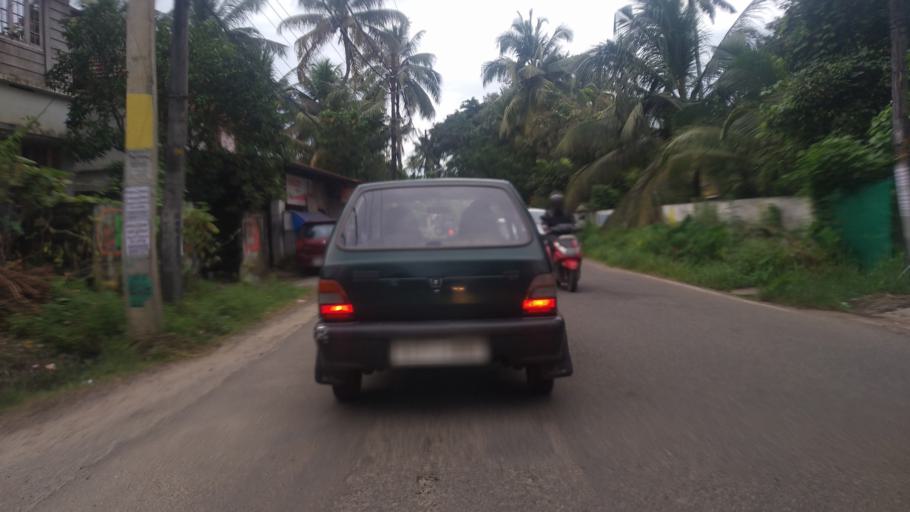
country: IN
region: Kerala
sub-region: Ernakulam
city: Cochin
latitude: 9.8827
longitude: 76.2621
